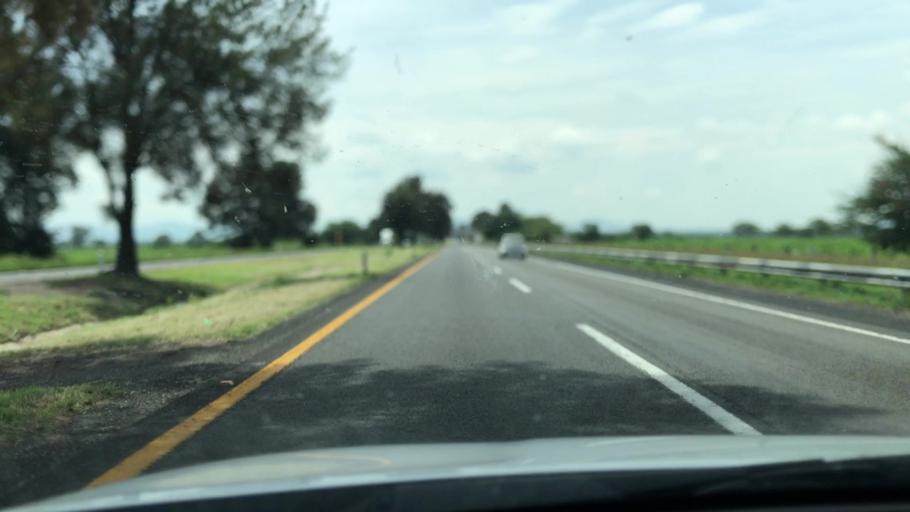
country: MX
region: Michoacan
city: Vistahermosa de Negrete
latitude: 20.2976
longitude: -102.4798
